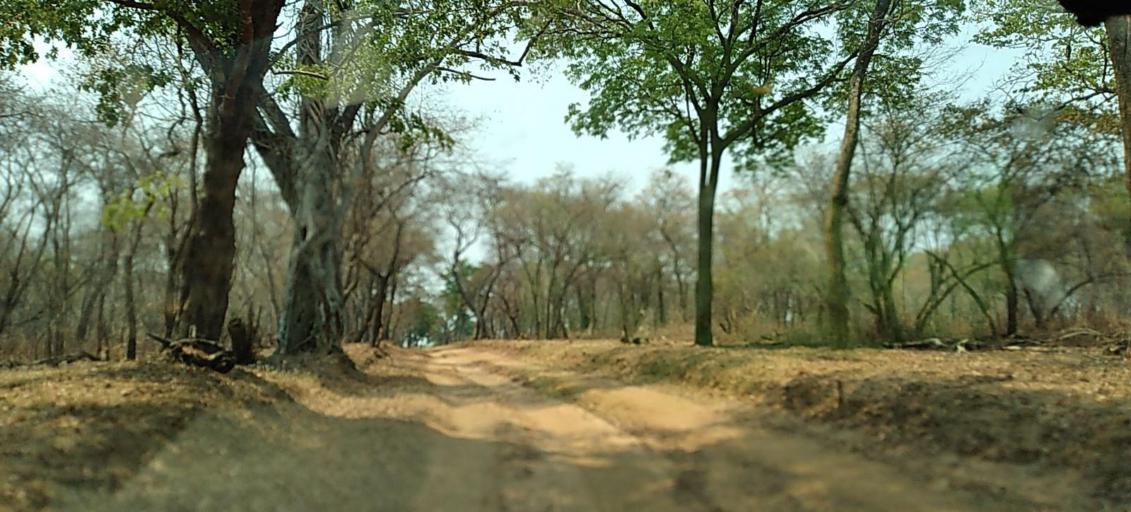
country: ZM
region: Western
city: Lukulu
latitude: -13.9861
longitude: 23.2289
